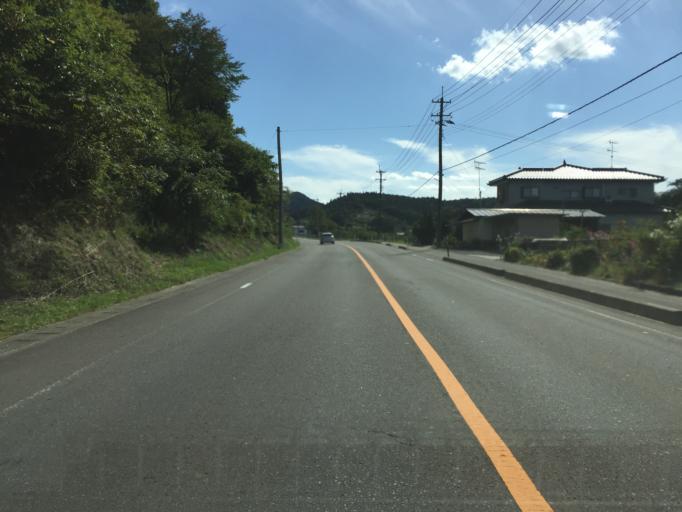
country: JP
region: Fukushima
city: Hobaramachi
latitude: 37.7998
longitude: 140.5736
